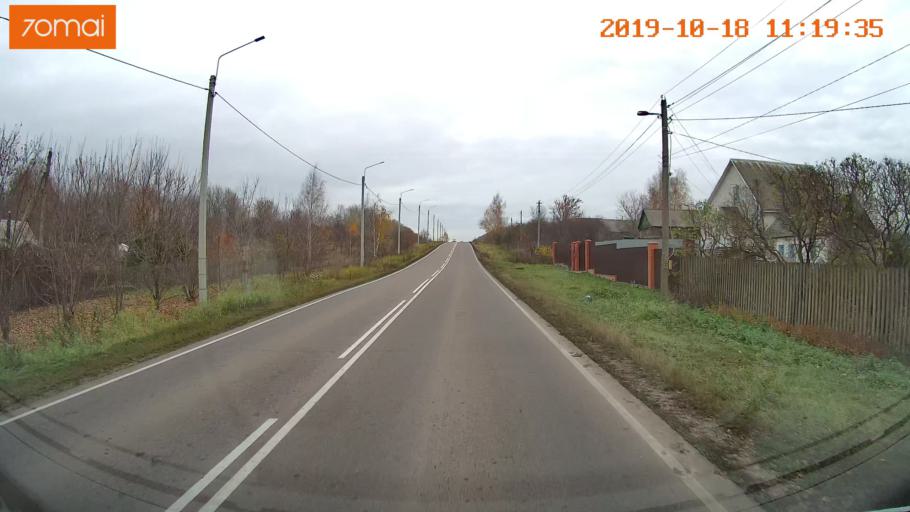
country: RU
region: Tula
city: Kimovsk
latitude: 54.0480
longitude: 38.5546
